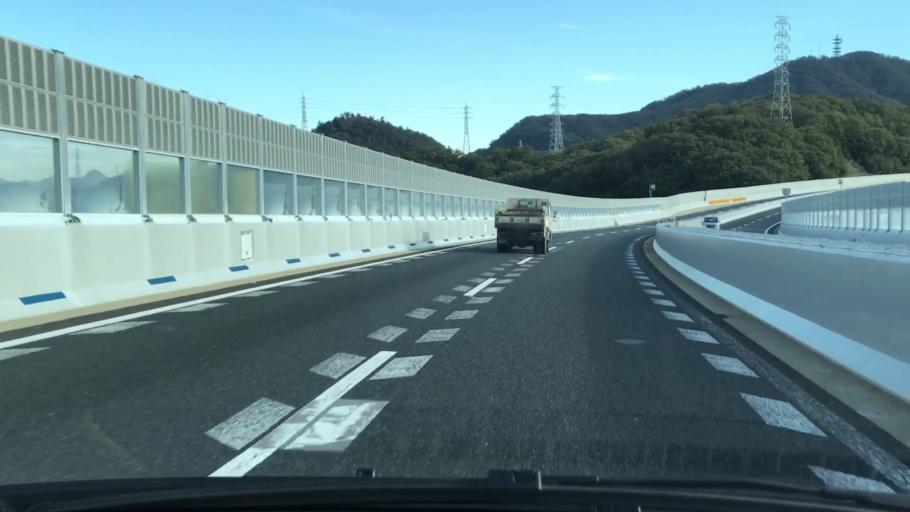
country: JP
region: Hyogo
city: Sandacho
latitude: 34.8170
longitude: 135.2481
